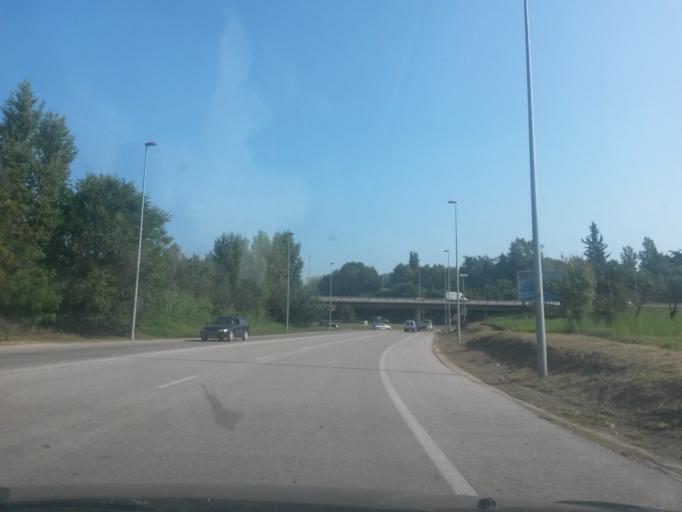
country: ES
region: Catalonia
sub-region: Provincia de Girona
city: Fornells de la Selva
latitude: 41.9555
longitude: 2.8087
